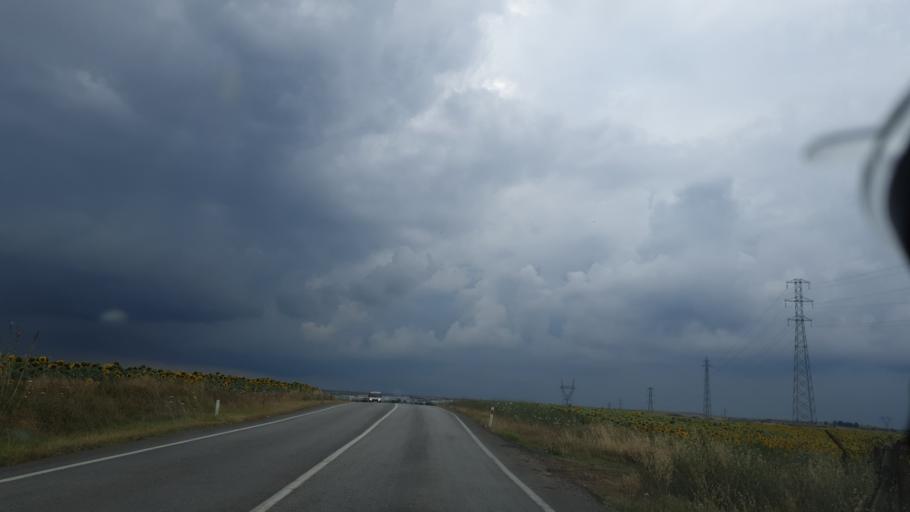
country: TR
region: Tekirdag
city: Hayrabolu
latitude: 41.2179
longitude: 27.0863
